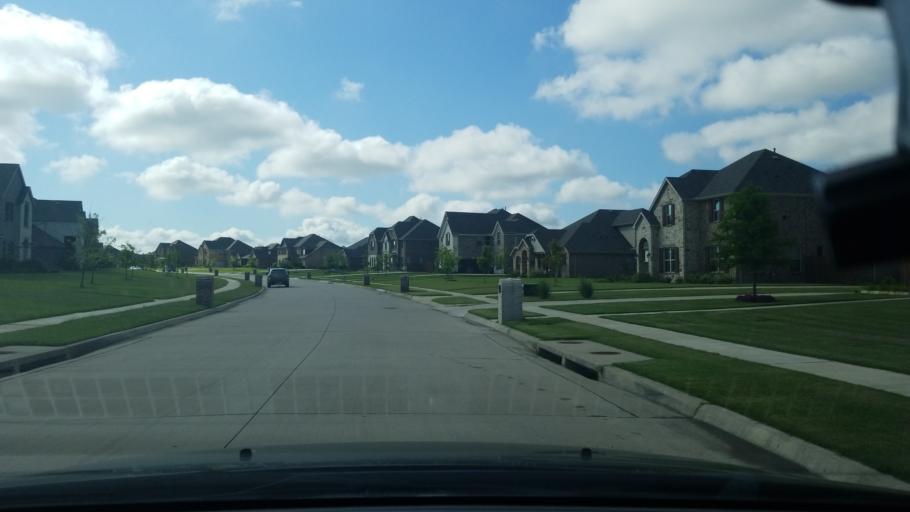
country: US
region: Texas
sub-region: Dallas County
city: Sunnyvale
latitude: 32.8018
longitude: -96.5658
